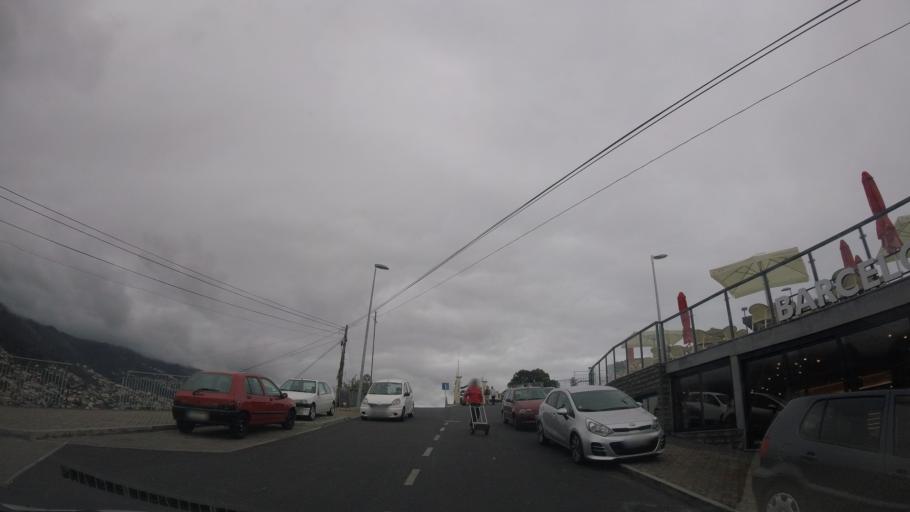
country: PT
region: Madeira
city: Camara de Lobos
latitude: 32.6593
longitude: -16.9405
